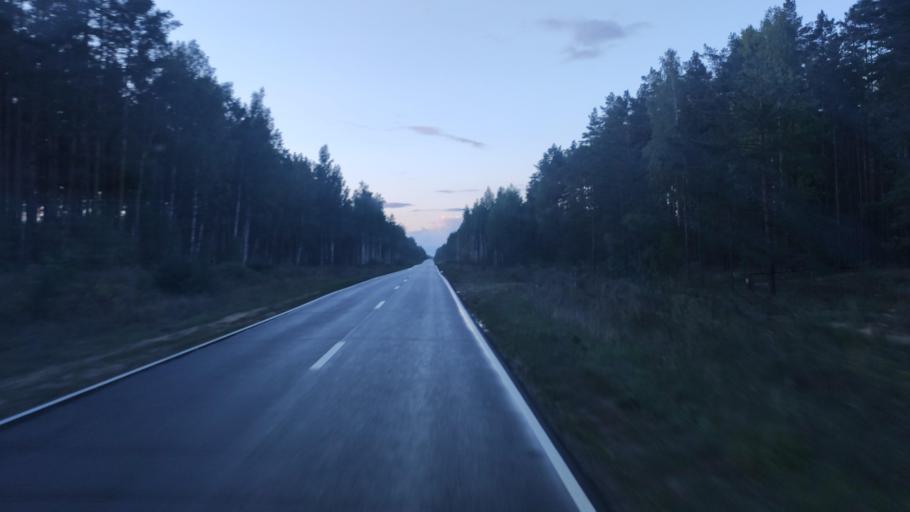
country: RU
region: Vladimir
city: Galitsy
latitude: 56.0679
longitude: 42.8667
